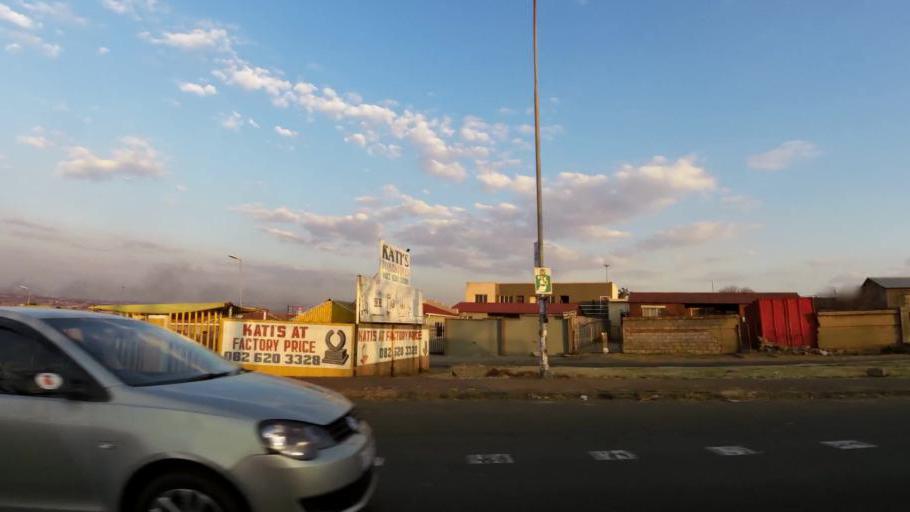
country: ZA
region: Gauteng
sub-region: City of Johannesburg Metropolitan Municipality
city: Soweto
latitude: -26.2360
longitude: 27.9037
